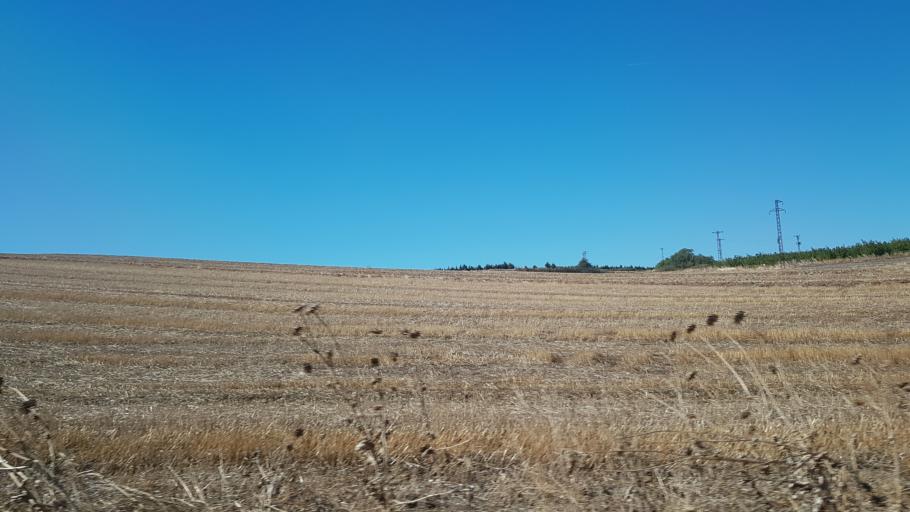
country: TR
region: Tekirdag
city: Corlu
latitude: 41.0346
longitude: 27.8145
